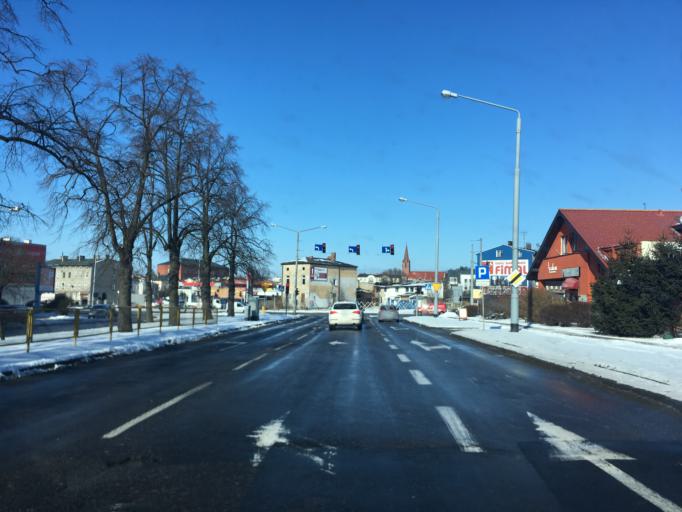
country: PL
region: Pomeranian Voivodeship
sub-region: Slupsk
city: Slupsk
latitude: 54.4642
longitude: 17.0416
